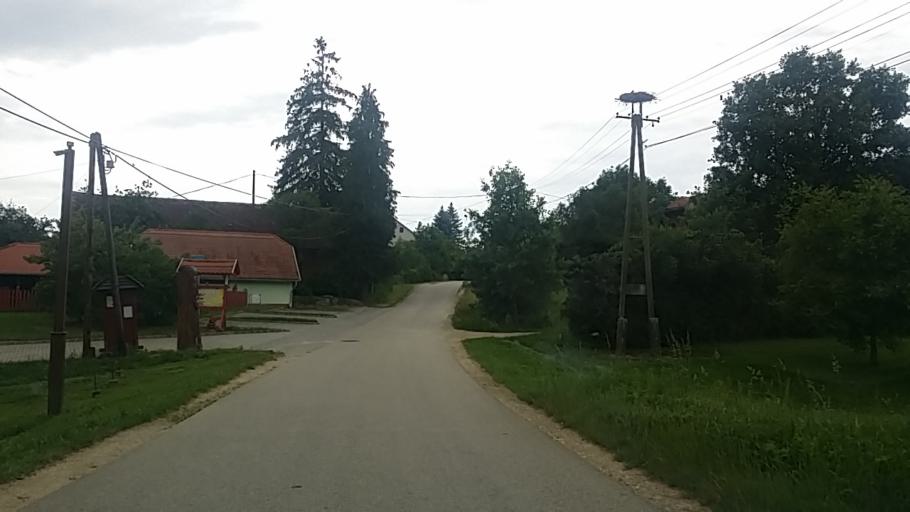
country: SI
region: Hodos-Hodos
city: Hodos
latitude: 46.8474
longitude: 16.4139
